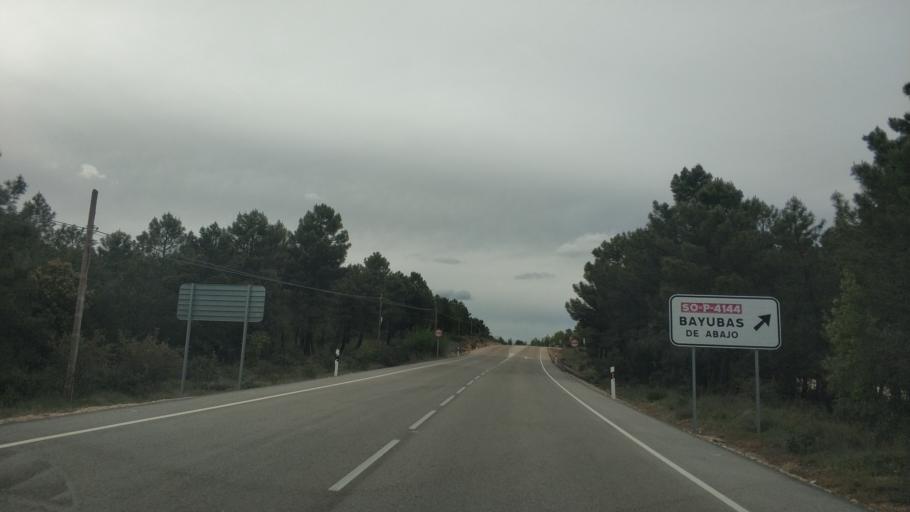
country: ES
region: Castille and Leon
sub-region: Provincia de Soria
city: Valdenebro
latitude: 41.5384
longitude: -2.9531
